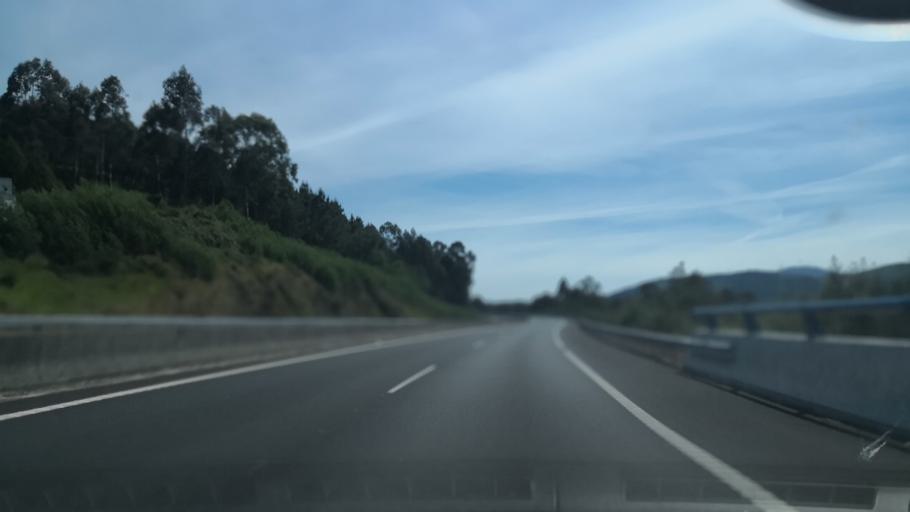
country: ES
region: Galicia
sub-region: Provincia de Pontevedra
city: Valga
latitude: 42.7131
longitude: -8.6438
